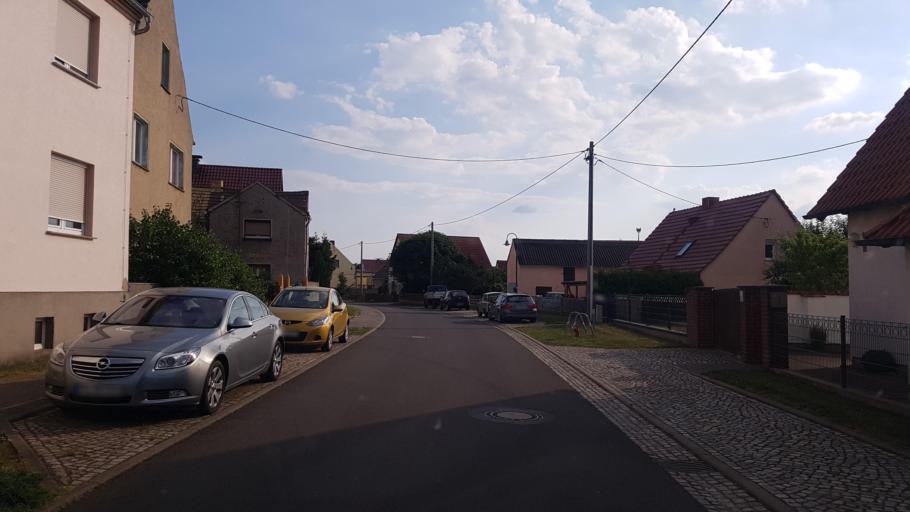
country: DE
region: Saxony
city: Torgau
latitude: 51.6373
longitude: 13.0067
